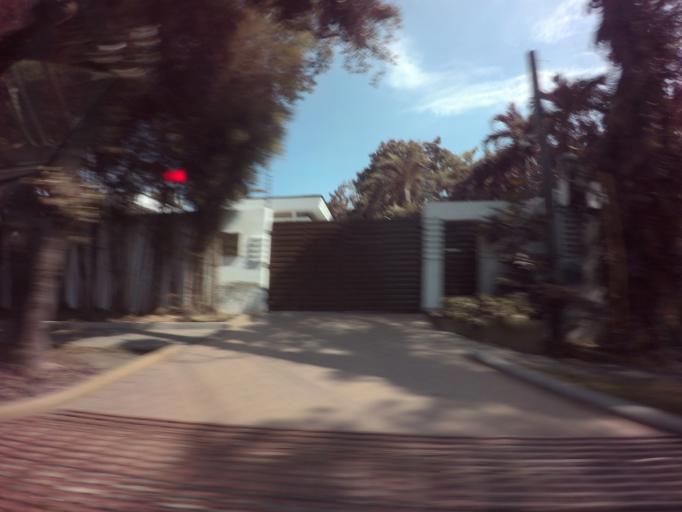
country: PH
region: Metro Manila
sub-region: Makati City
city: Makati City
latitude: 14.5476
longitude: 121.0396
